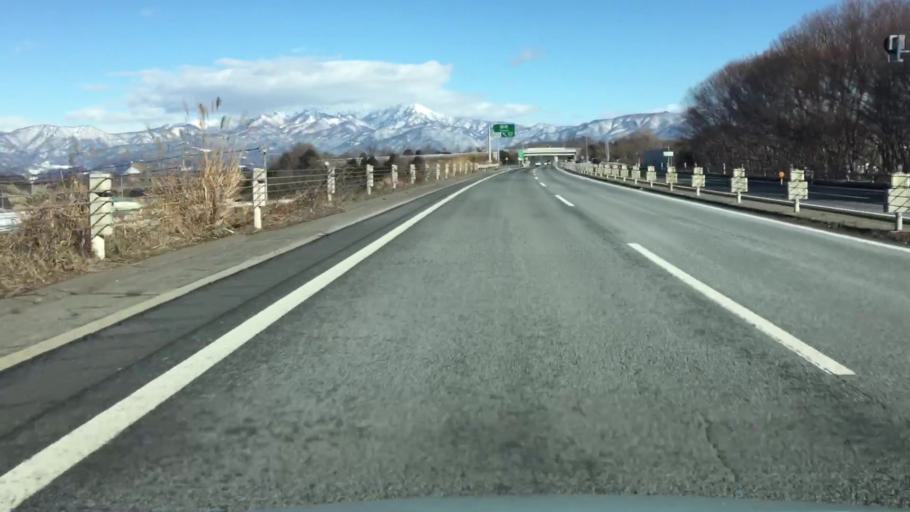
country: JP
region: Gunma
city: Numata
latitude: 36.6119
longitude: 139.0648
